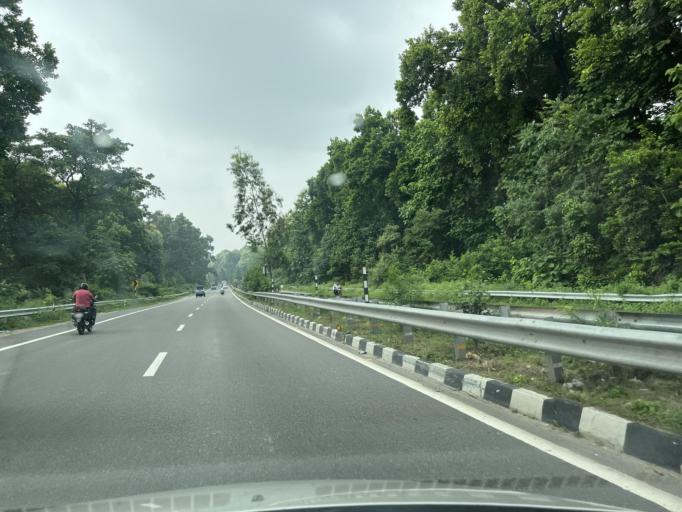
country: IN
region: Uttarakhand
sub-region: Dehradun
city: Raiwala
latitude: 30.0240
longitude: 78.2038
